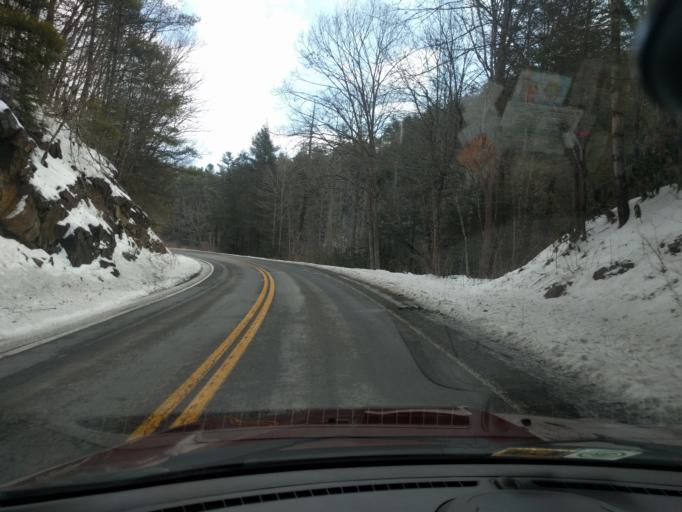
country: US
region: West Virginia
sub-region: Pocahontas County
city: Marlinton
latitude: 38.1355
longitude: -79.9709
